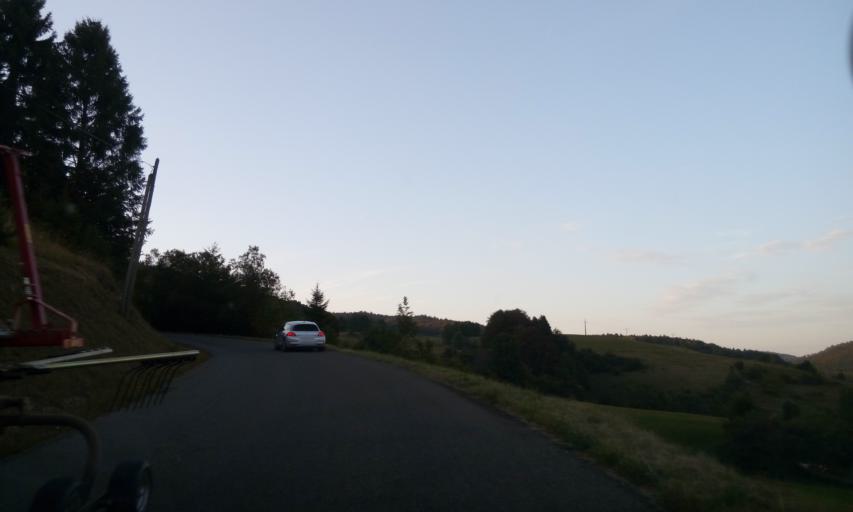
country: FR
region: Rhone-Alpes
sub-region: Departement de l'Ain
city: Nantua
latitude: 46.1864
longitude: 5.6779
